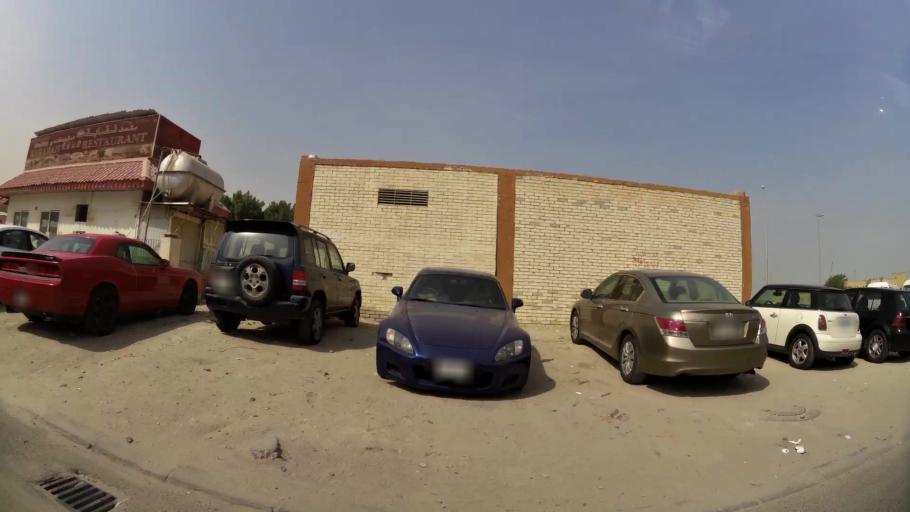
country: KW
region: Al Asimah
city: Ash Shamiyah
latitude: 29.3343
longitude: 47.9499
